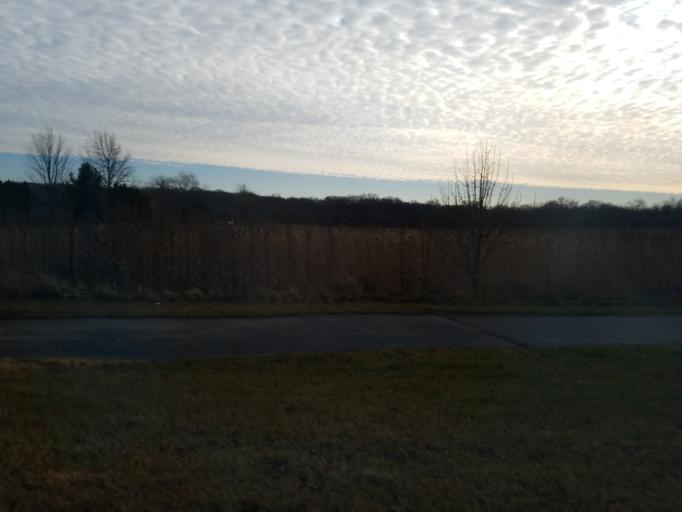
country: US
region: Illinois
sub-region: Will County
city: Mokena
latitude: 41.5282
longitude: -87.8602
